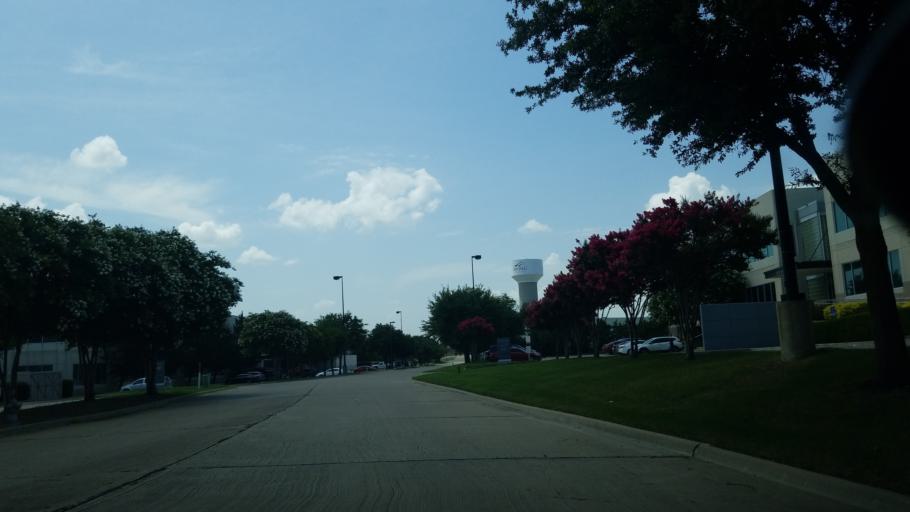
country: US
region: Texas
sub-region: Dallas County
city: Coppell
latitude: 32.9162
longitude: -96.9953
